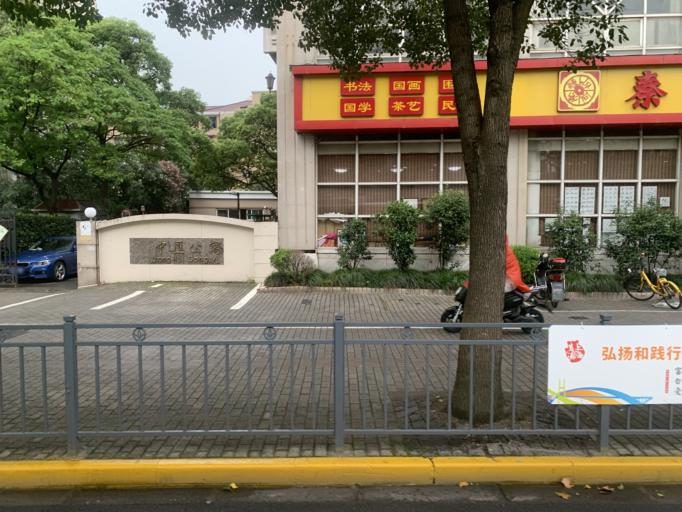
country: CN
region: Shanghai Shi
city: Luwan
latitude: 31.2120
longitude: 121.4752
